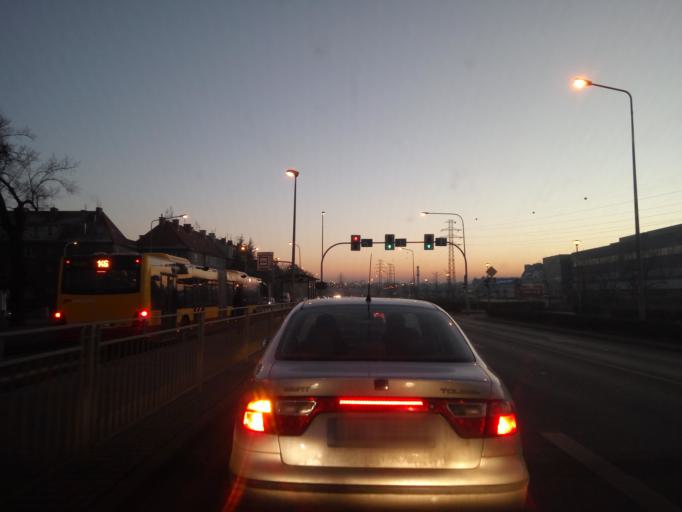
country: PL
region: Lower Silesian Voivodeship
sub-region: Powiat wroclawski
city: Wroclaw
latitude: 51.0779
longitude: 17.0338
